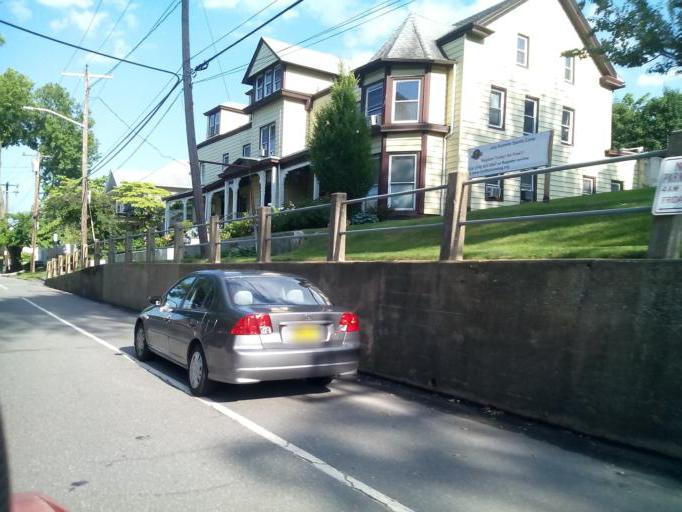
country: US
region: New York
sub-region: Nassau County
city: Oyster Bay
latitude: 40.8724
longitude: -73.5344
